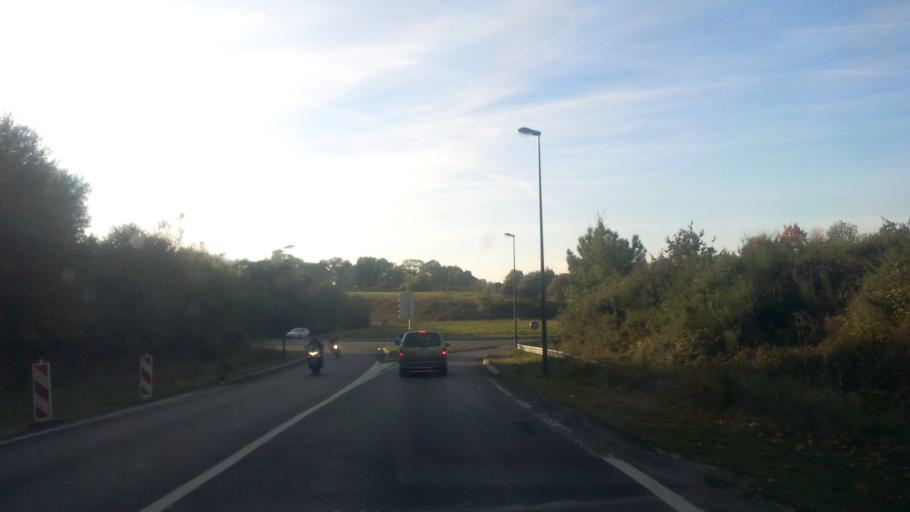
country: FR
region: Brittany
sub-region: Departement du Morbihan
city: Elven
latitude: 47.7230
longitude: -2.5897
